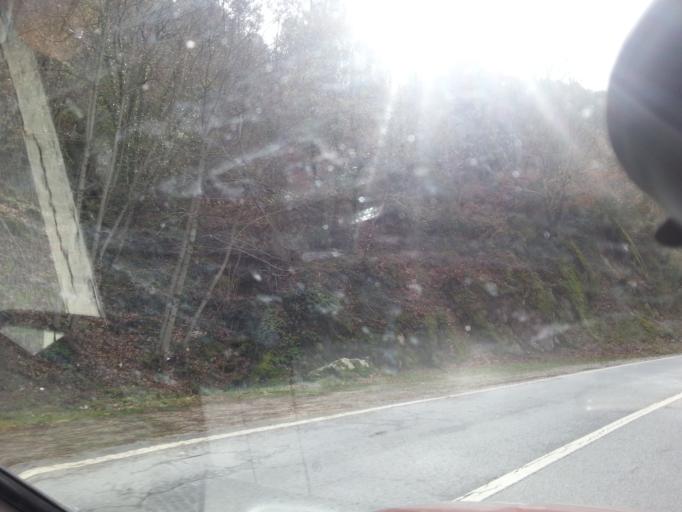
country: PT
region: Guarda
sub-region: Seia
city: Seia
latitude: 40.3731
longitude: -7.7126
